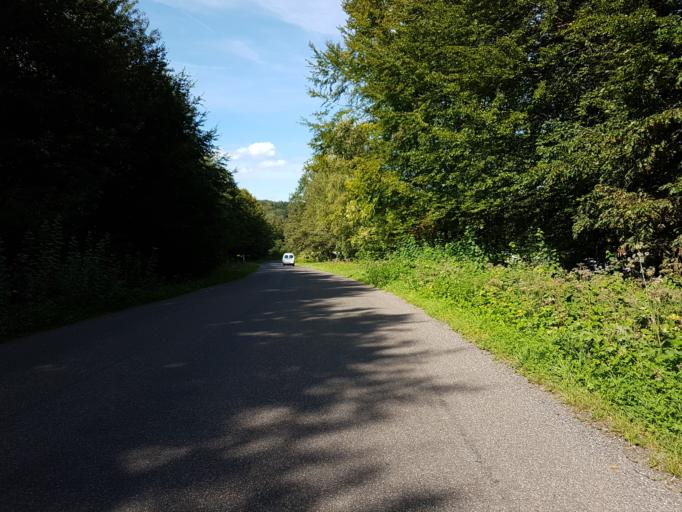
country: FR
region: Franche-Comte
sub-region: Departement de la Haute-Saone
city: Luxeuil-les-Bains
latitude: 47.8243
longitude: 6.3642
